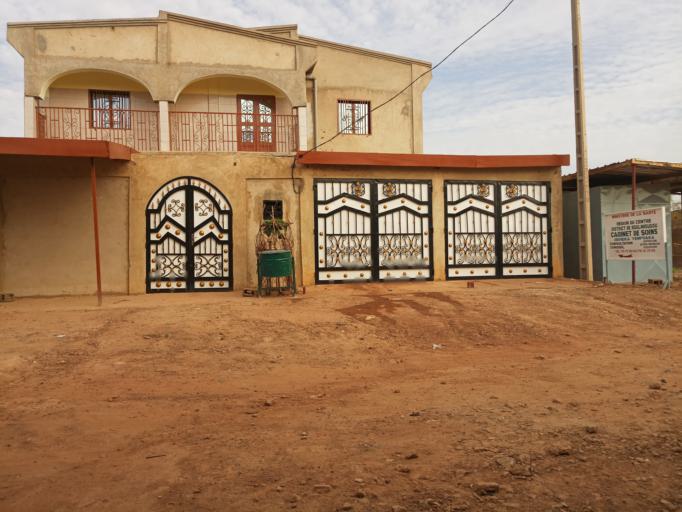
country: BF
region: Centre
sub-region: Kadiogo Province
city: Ouagadougou
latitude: 12.2539
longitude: -1.5209
